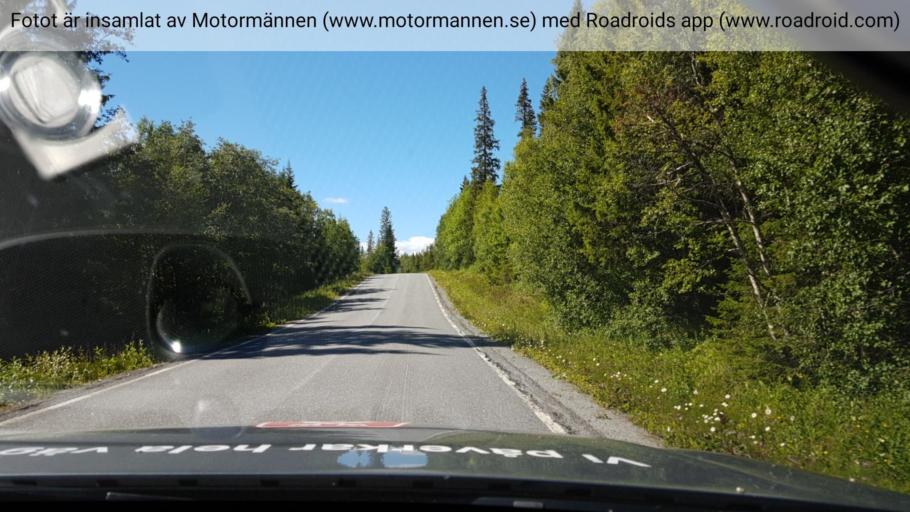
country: SE
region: Jaemtland
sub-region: Are Kommun
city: Are
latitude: 63.3146
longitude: 13.1479
